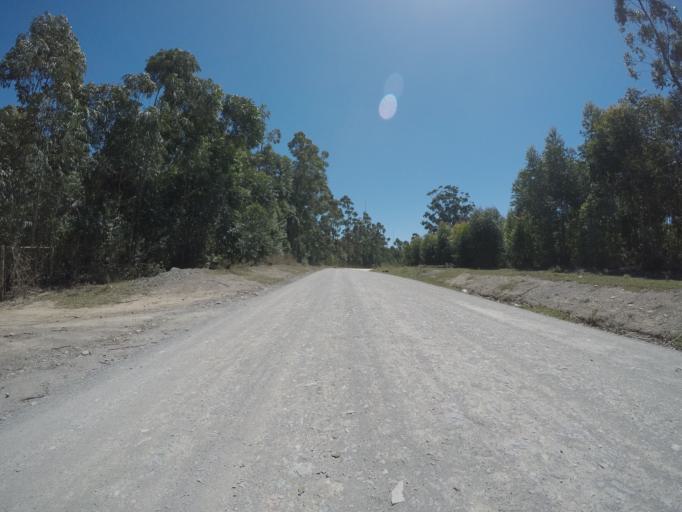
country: ZA
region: Eastern Cape
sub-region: OR Tambo District Municipality
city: Libode
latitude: -31.9583
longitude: 29.0238
